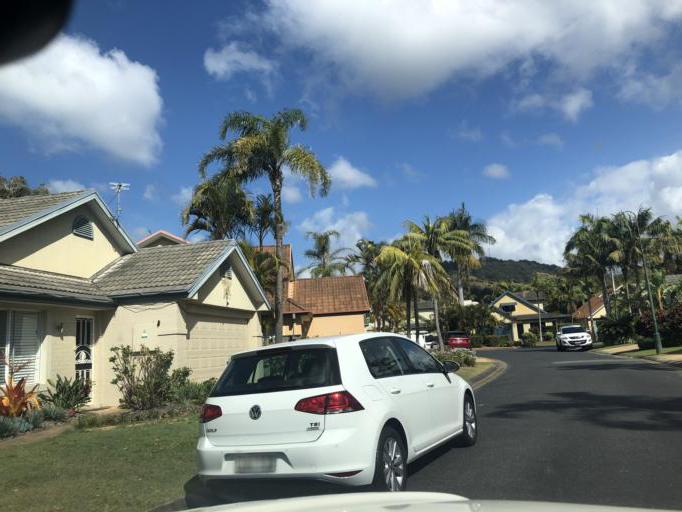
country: AU
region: New South Wales
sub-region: Coffs Harbour
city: Moonee Beach
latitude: -30.2302
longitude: 153.1520
